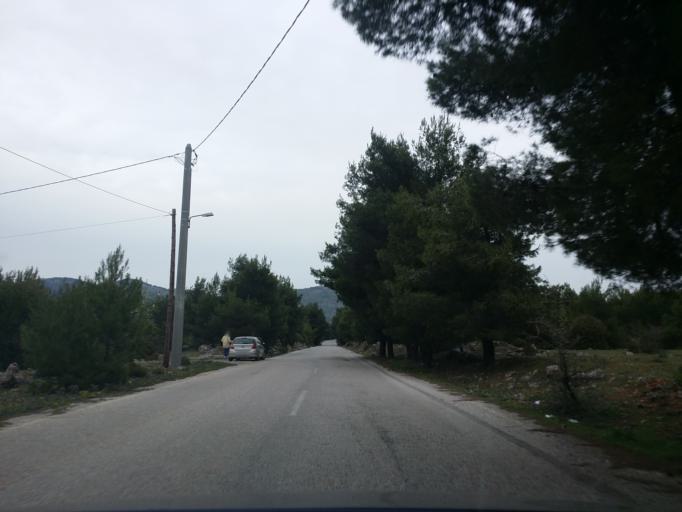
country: GR
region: Attica
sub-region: Nomarchia Dytikis Attikis
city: Vilia
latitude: 38.1479
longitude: 23.2964
